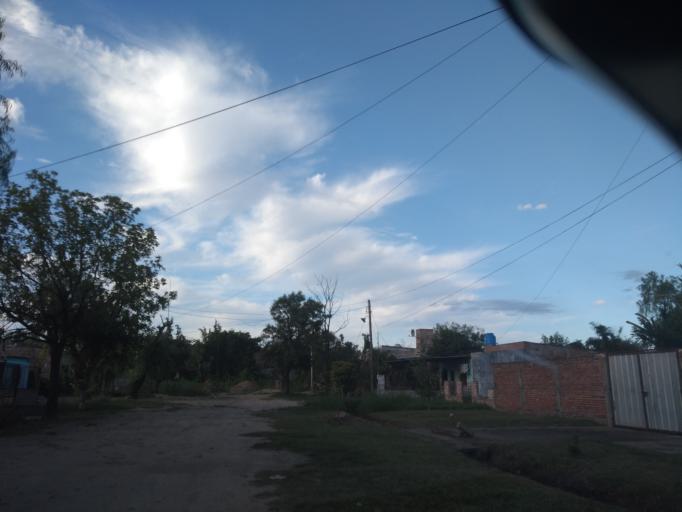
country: AR
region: Chaco
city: Barranqueras
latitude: -27.4811
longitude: -58.9271
